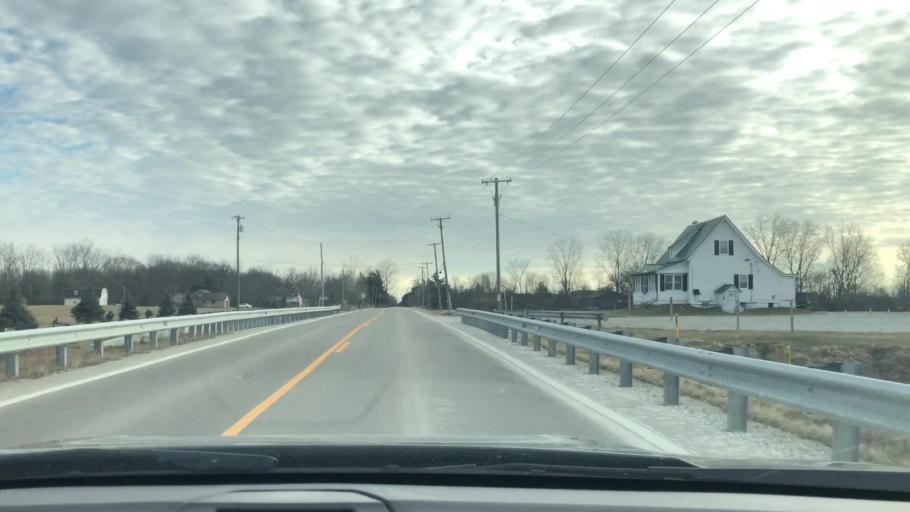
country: US
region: Michigan
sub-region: Macomb County
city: Romeo
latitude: 42.7307
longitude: -82.9760
